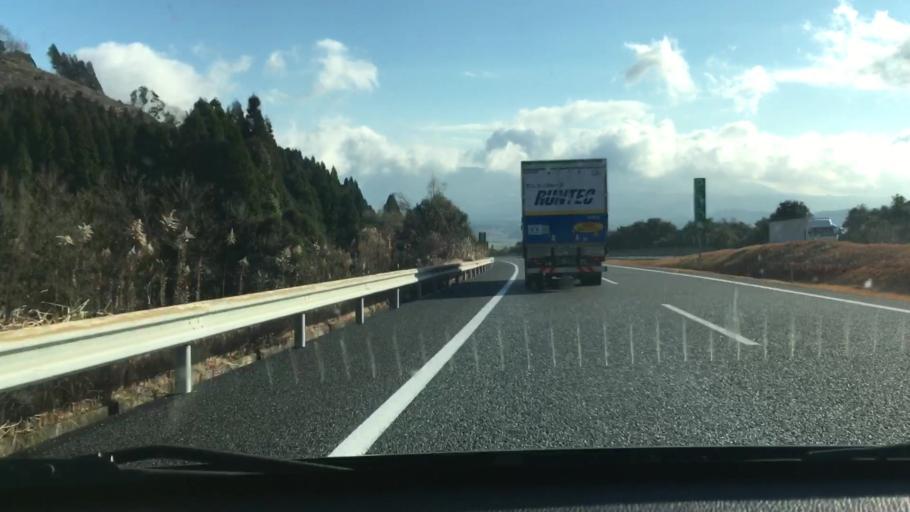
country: JP
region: Kumamoto
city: Hitoyoshi
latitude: 32.0751
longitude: 130.7930
